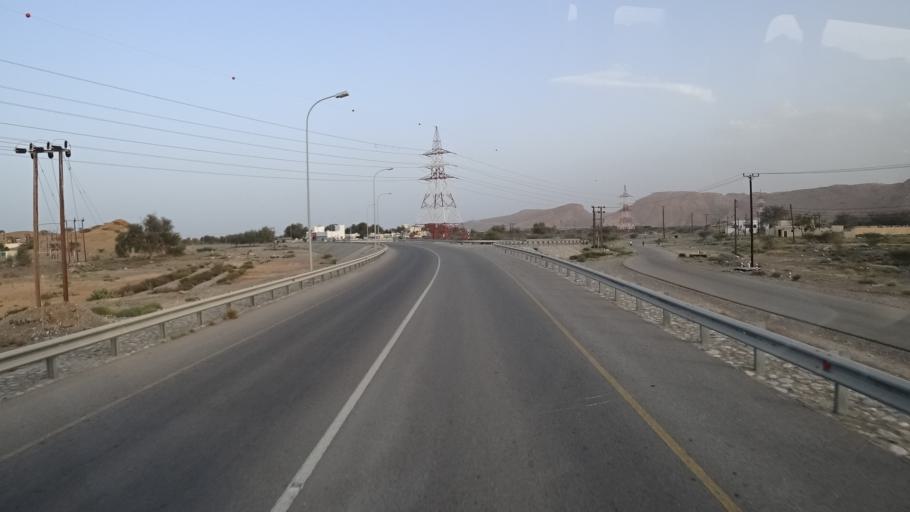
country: OM
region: Muhafazat Masqat
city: Muscat
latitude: 23.2059
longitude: 58.9499
